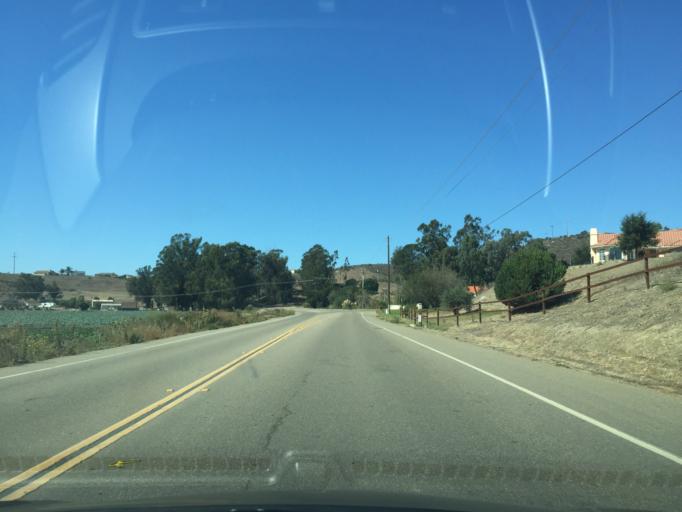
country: US
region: California
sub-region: Santa Barbara County
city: Mission Hills
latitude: 34.6764
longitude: -120.4447
